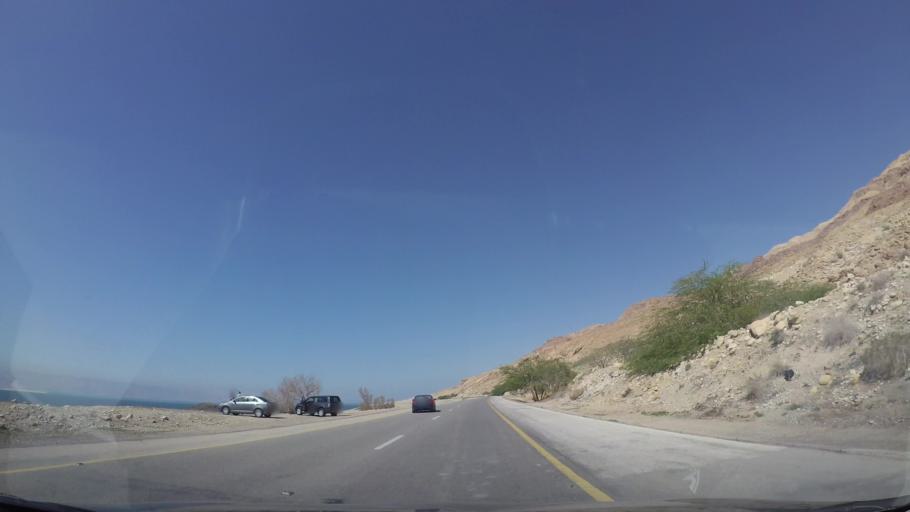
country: JO
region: Karak
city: Al Qasr
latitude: 31.3553
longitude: 35.5480
